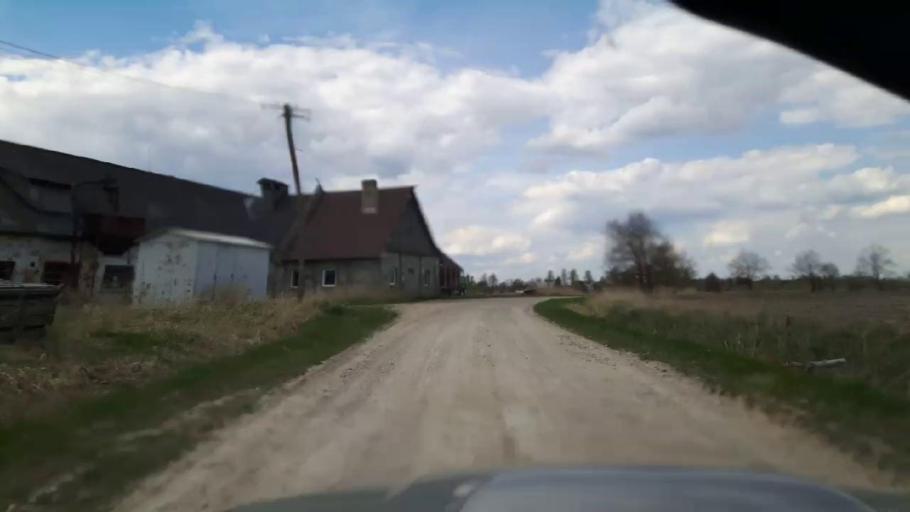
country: EE
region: Paernumaa
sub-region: Sindi linn
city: Sindi
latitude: 58.4129
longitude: 24.6959
